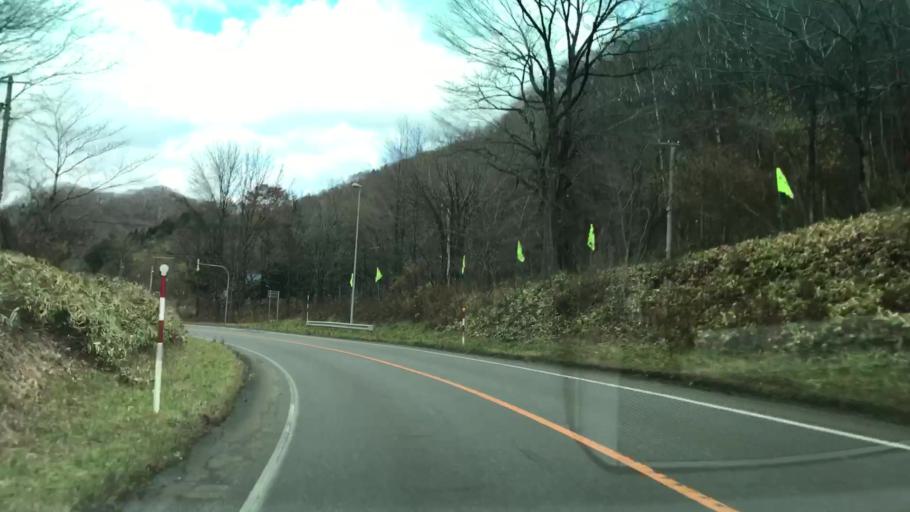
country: JP
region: Hokkaido
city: Shizunai-furukawacho
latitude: 42.8159
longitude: 142.4215
